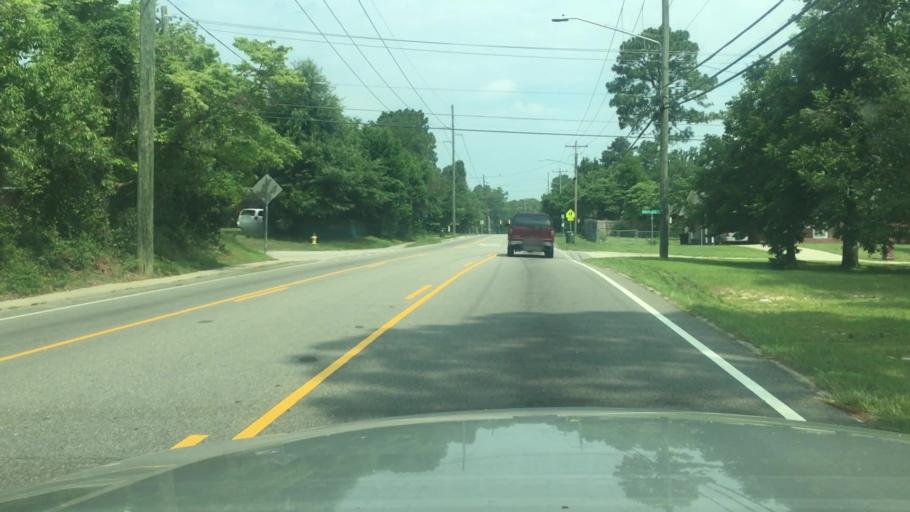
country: US
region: North Carolina
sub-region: Cumberland County
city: Hope Mills
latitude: 35.0283
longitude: -78.9444
